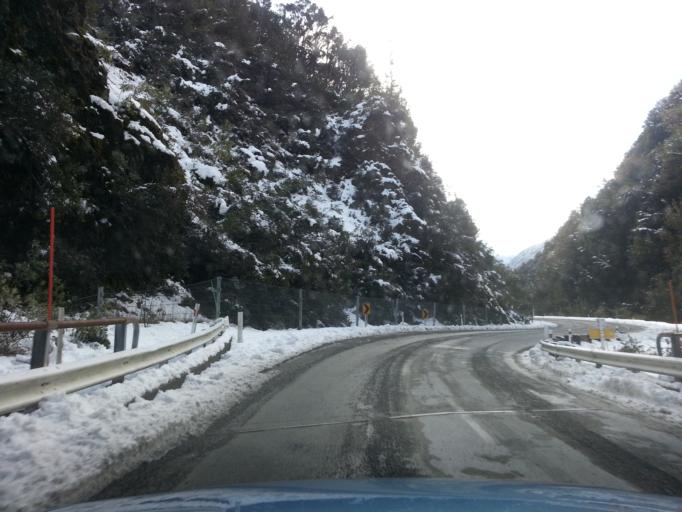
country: NZ
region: West Coast
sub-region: Grey District
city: Greymouth
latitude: -42.8710
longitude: 171.5548
